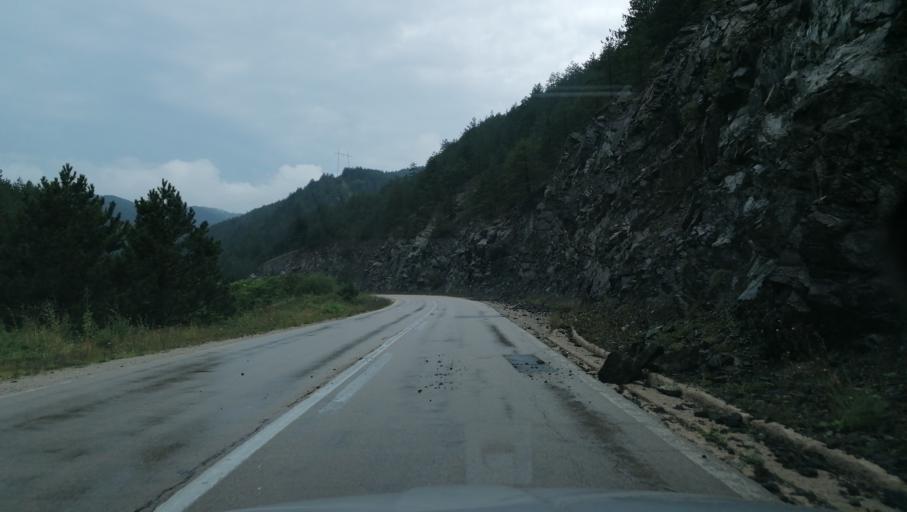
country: RS
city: Durici
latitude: 43.8308
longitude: 19.5326
